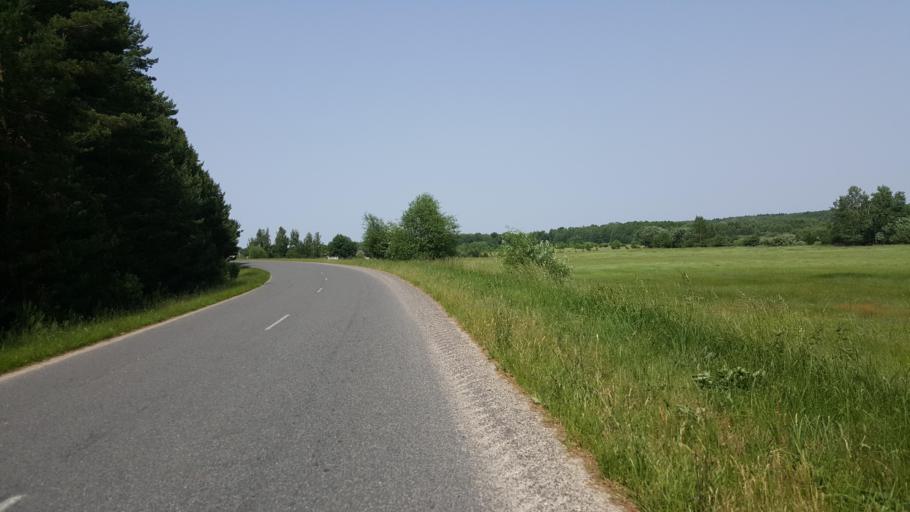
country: BY
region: Brest
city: Kamyanyuki
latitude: 52.5157
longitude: 23.8529
